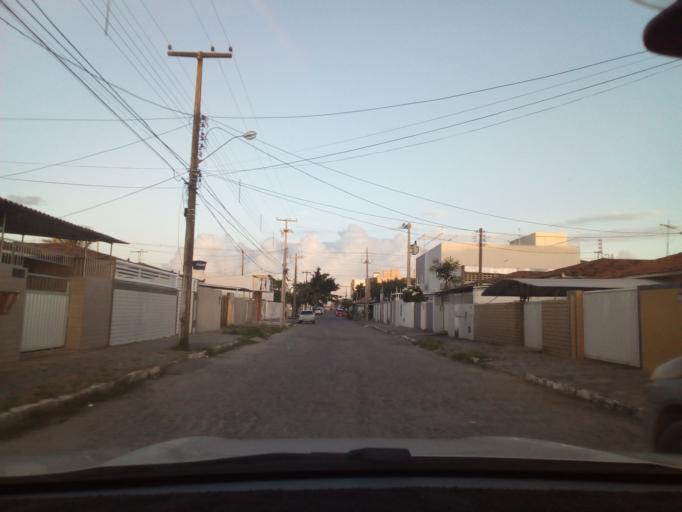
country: BR
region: Paraiba
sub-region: Joao Pessoa
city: Joao Pessoa
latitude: -7.1645
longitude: -34.8699
